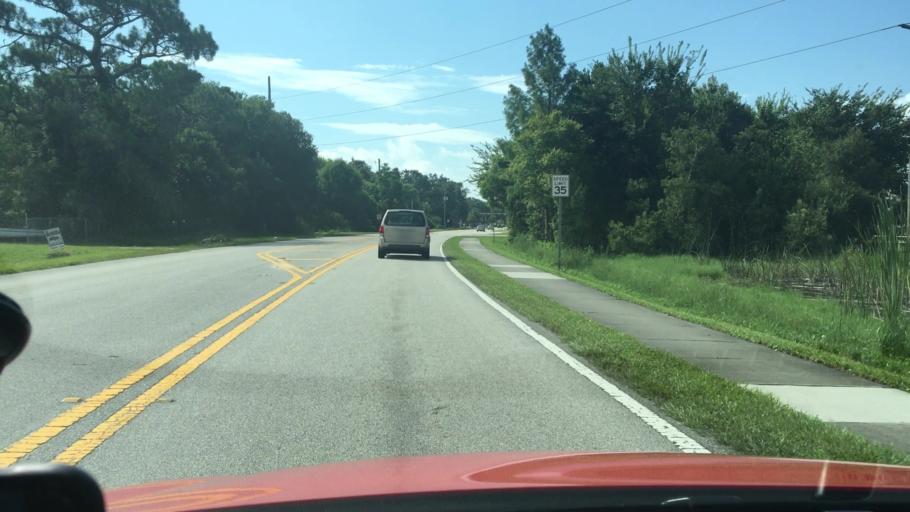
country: US
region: Florida
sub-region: Volusia County
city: New Smyrna Beach
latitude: 29.0177
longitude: -80.9441
